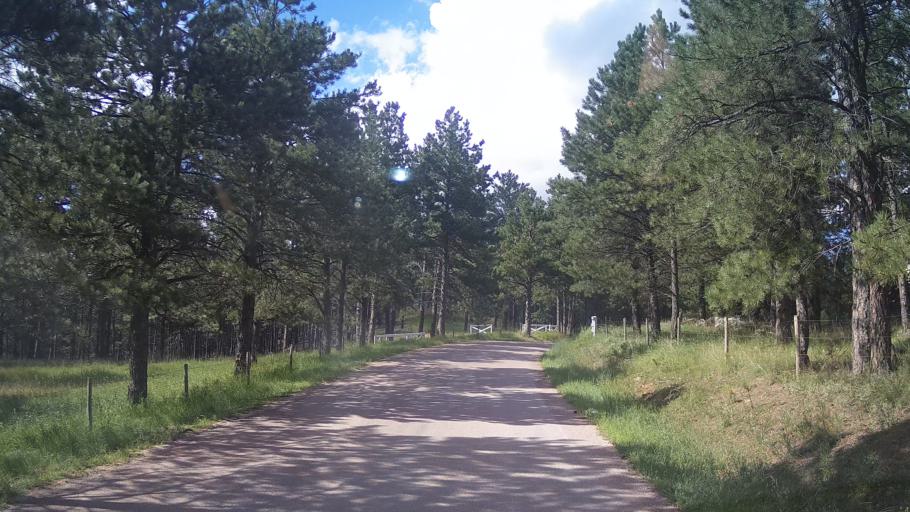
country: US
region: South Dakota
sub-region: Pennington County
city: Colonial Pine Hills
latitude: 43.8531
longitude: -103.3829
